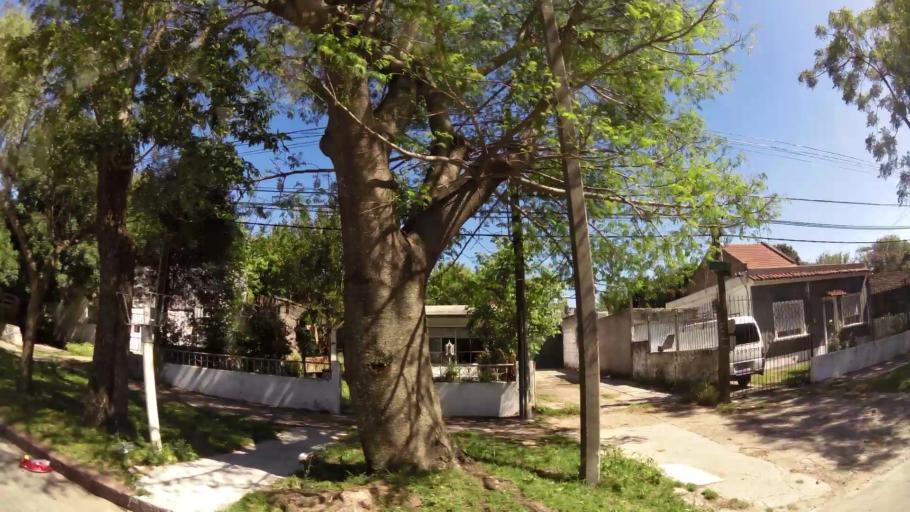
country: UY
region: Canelones
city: Paso de Carrasco
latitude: -34.8675
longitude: -56.1221
